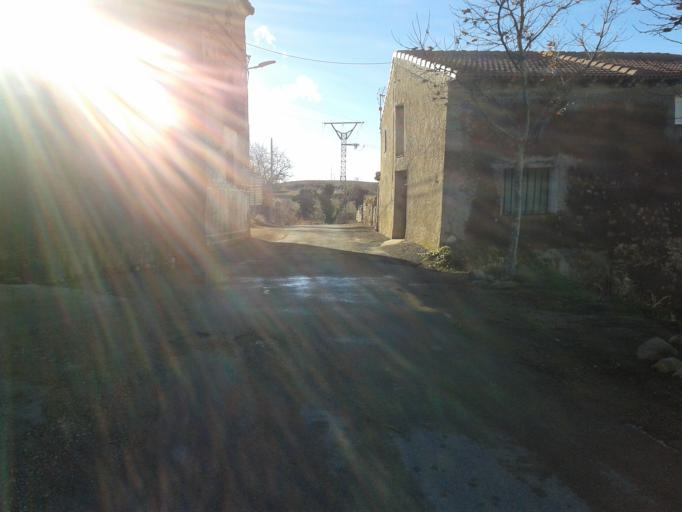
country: ES
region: Aragon
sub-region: Provincia de Teruel
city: Bea
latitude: 40.9897
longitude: -1.1642
